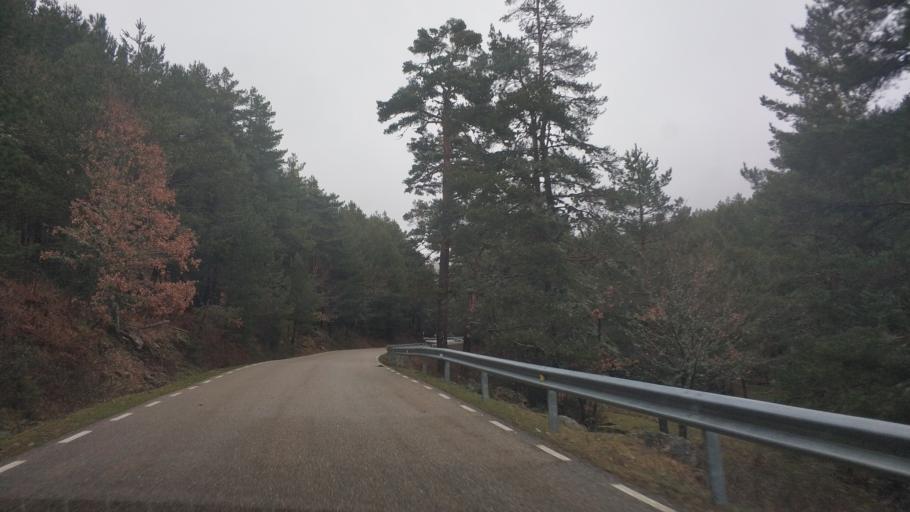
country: ES
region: Castille and Leon
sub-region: Provincia de Burgos
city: Neila
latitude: 42.0270
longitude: -3.0110
